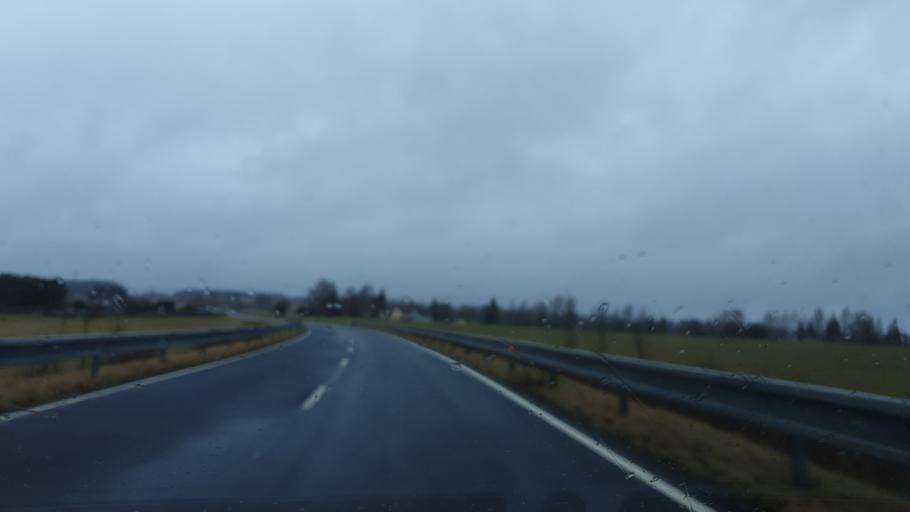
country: CZ
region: Karlovarsky
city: Hranice
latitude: 50.2946
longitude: 12.1777
